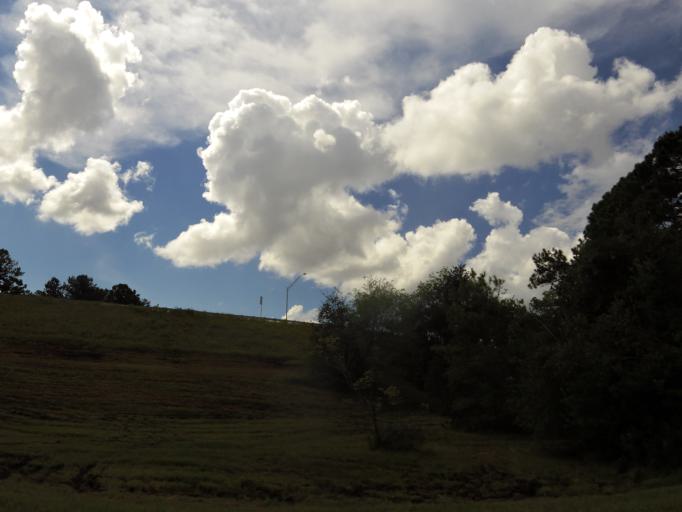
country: US
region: Florida
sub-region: Duval County
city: Jacksonville
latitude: 30.3176
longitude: -81.7682
